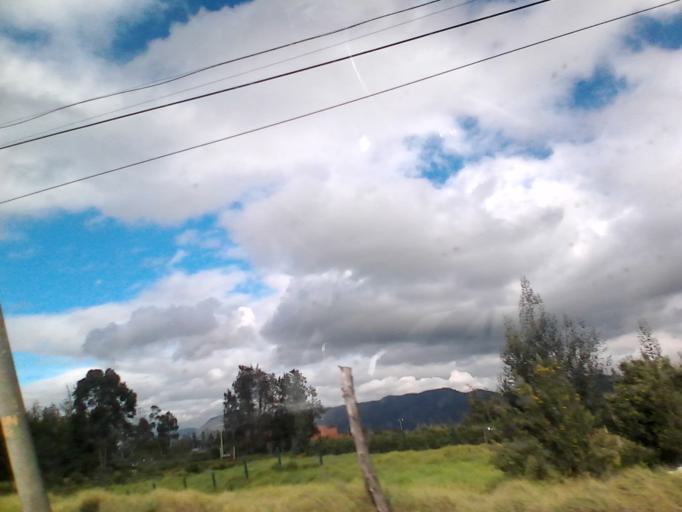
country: CO
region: Cundinamarca
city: Chia
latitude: 4.8593
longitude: -74.0288
